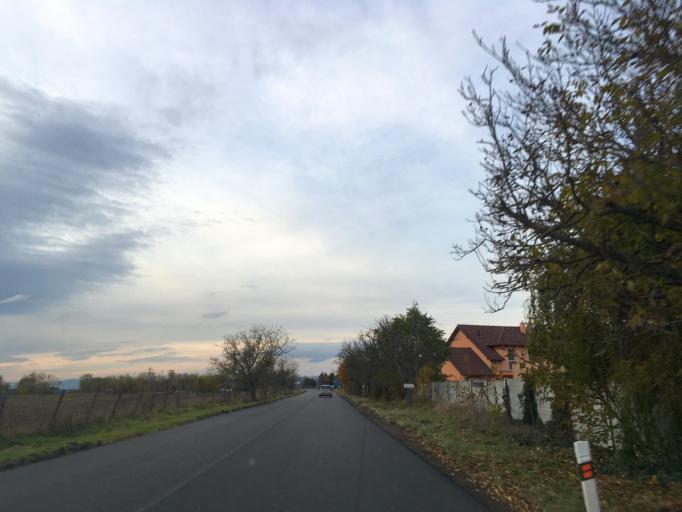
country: SK
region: Bratislavsky
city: Dunajska Luzna
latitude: 48.1256
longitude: 17.2974
